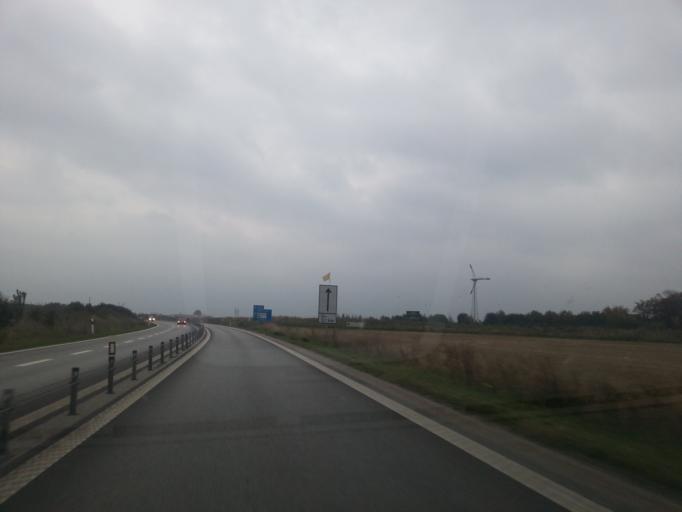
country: SE
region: Skane
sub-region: Staffanstorps Kommun
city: Hjaerup
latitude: 55.7067
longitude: 13.1448
